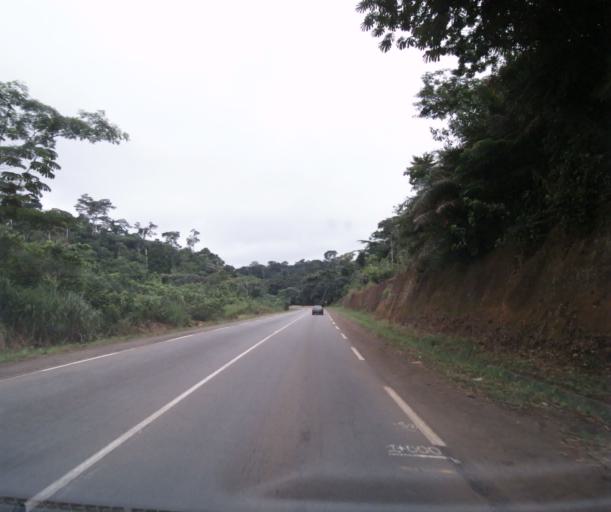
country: CM
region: Centre
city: Mbankomo
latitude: 3.7822
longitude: 11.2622
